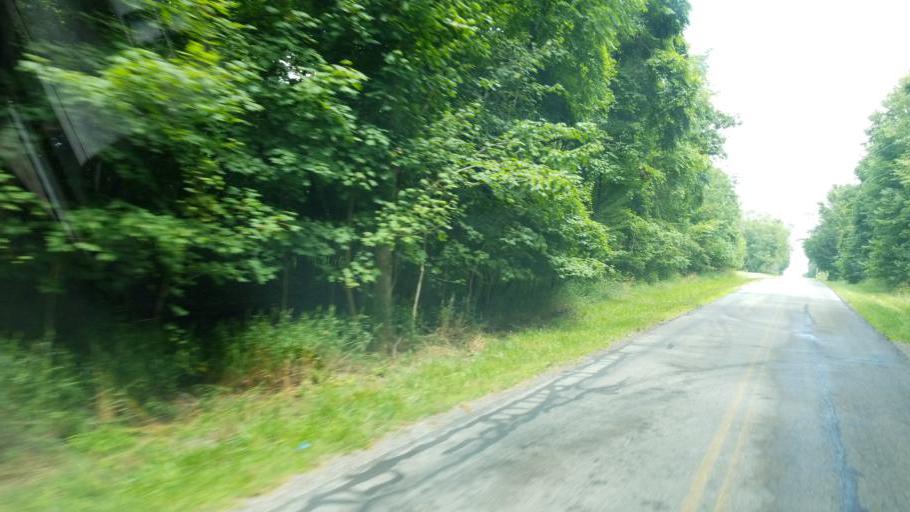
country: US
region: Ohio
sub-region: Logan County
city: Northwood
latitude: 40.4137
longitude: -83.6777
